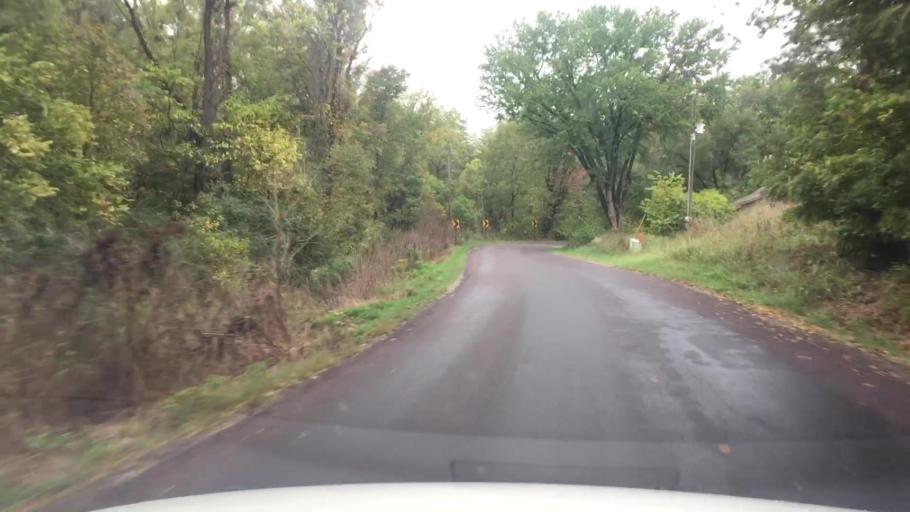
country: US
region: Missouri
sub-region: Boone County
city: Columbia
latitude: 38.8560
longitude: -92.3709
